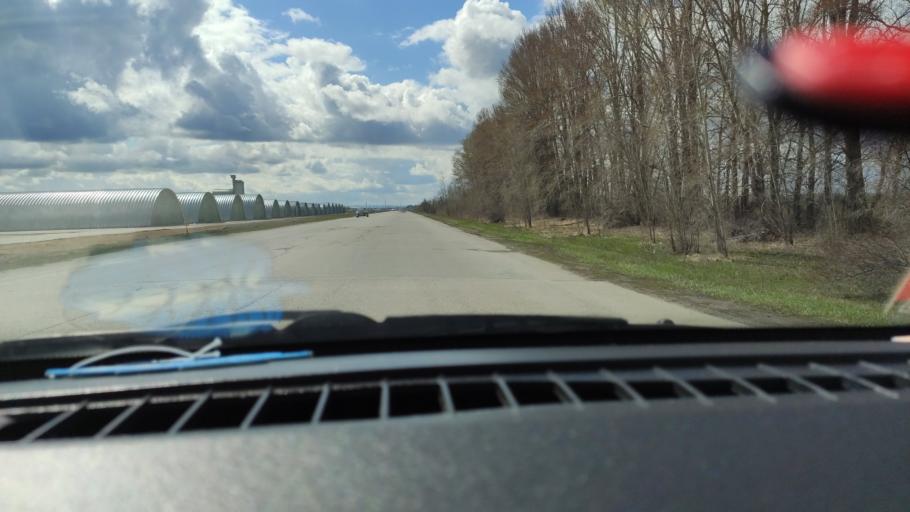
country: RU
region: Samara
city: Tol'yatti
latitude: 53.6867
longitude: 49.4173
